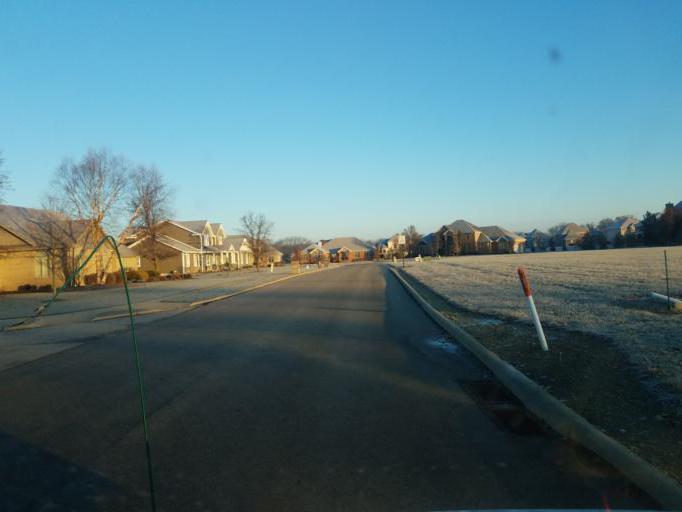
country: US
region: Ohio
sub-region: Marion County
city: Marion
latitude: 40.5649
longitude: -83.0954
